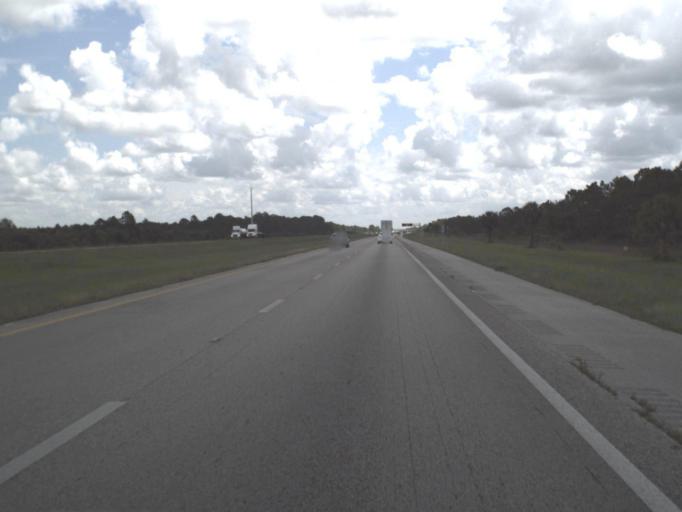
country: US
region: Florida
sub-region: Collier County
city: Golden Gate
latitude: 26.1530
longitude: -81.5671
